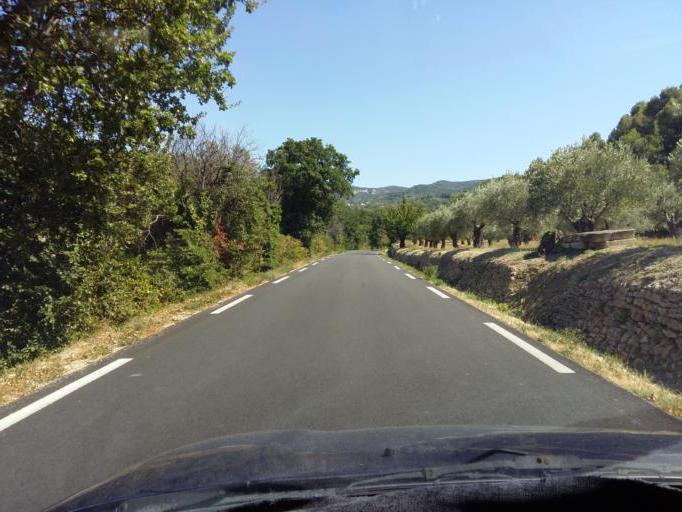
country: FR
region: Provence-Alpes-Cote d'Azur
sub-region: Departement du Vaucluse
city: Venasque
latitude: 44.0052
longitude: 5.1415
